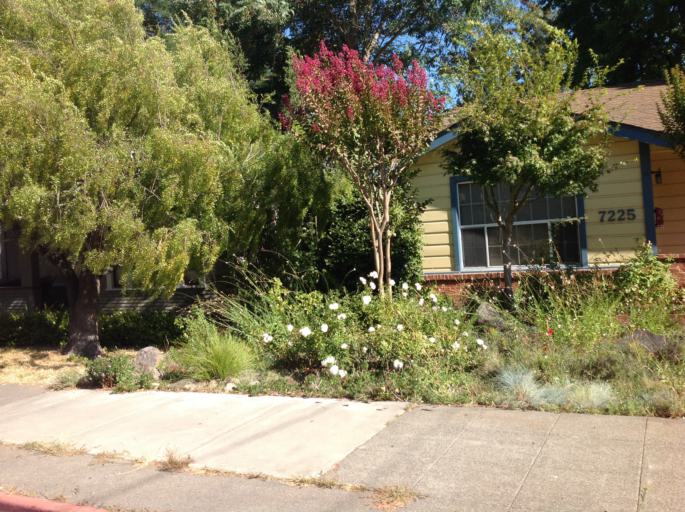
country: US
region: California
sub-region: Sonoma County
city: Sebastopol
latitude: 38.4014
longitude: -122.8261
